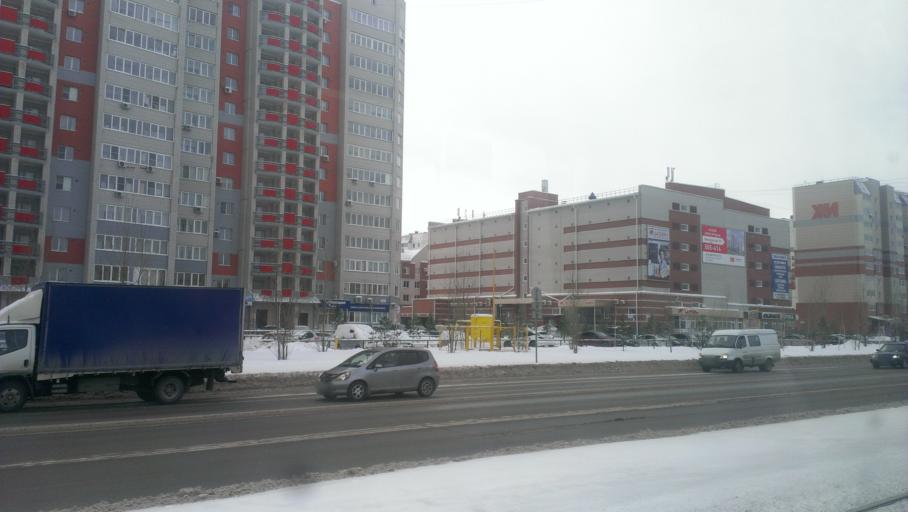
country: RU
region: Altai Krai
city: Novosilikatnyy
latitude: 53.3287
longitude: 83.6792
